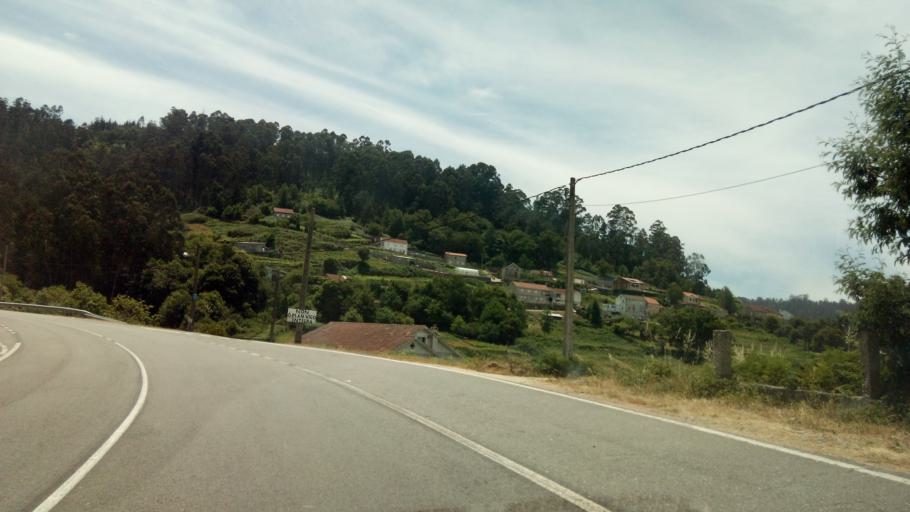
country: ES
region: Galicia
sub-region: Provincia de Pontevedra
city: Marin
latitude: 42.3519
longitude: -8.6980
